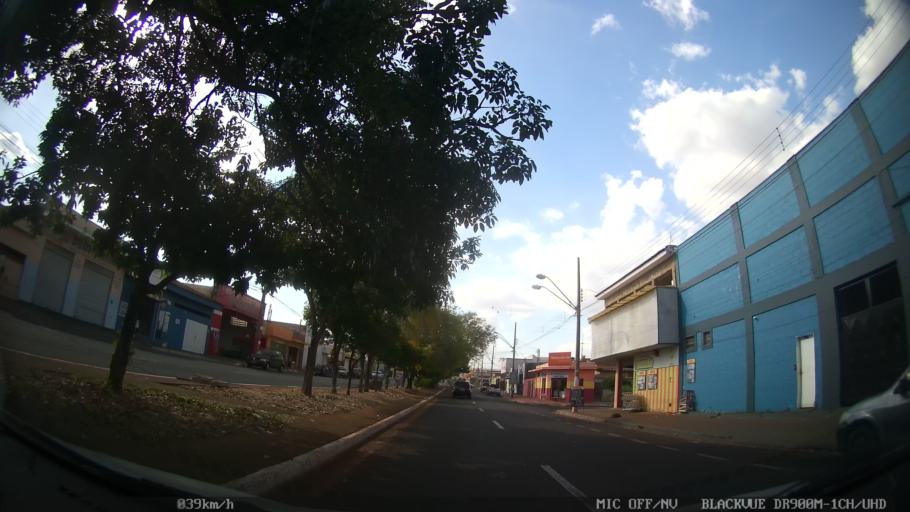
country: BR
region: Sao Paulo
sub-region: Ribeirao Preto
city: Ribeirao Preto
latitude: -21.1930
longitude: -47.8382
